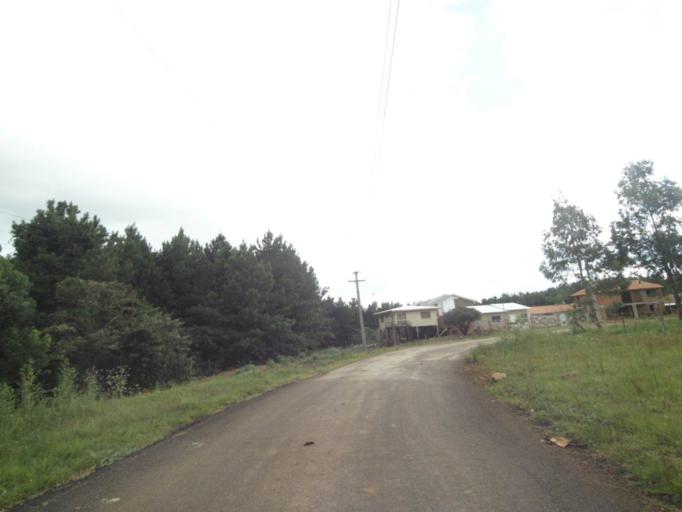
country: BR
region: Rio Grande do Sul
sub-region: Lagoa Vermelha
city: Lagoa Vermelha
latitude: -28.2048
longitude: -51.5095
